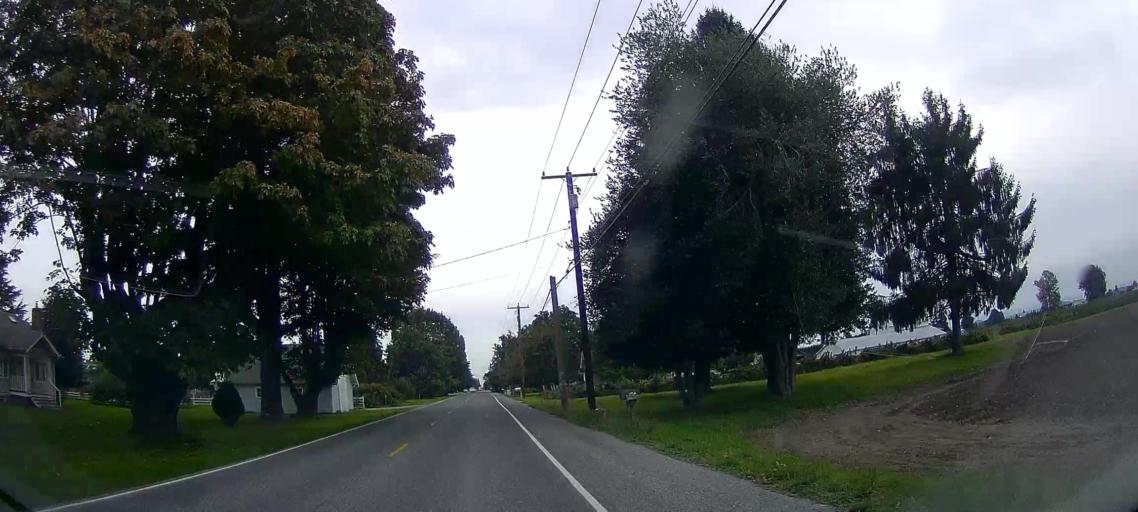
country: US
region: Washington
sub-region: Skagit County
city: Mount Vernon
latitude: 48.4487
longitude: -122.3787
